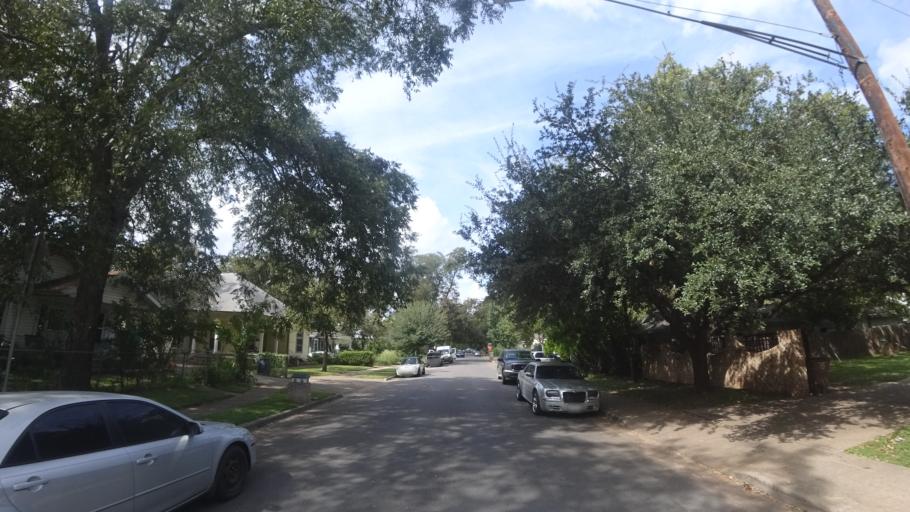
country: US
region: Texas
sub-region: Travis County
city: Austin
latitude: 30.2541
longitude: -97.7189
